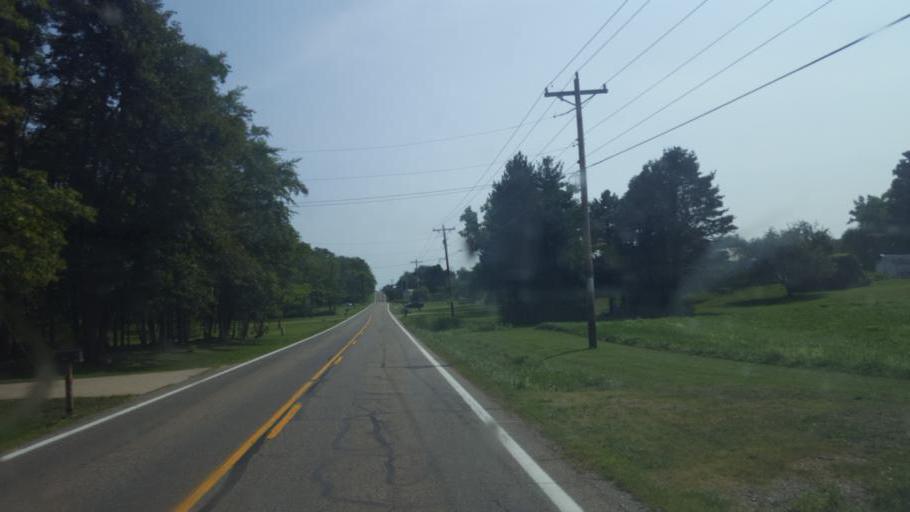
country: US
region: Ohio
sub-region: Richland County
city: Lexington
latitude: 40.6709
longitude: -82.6640
